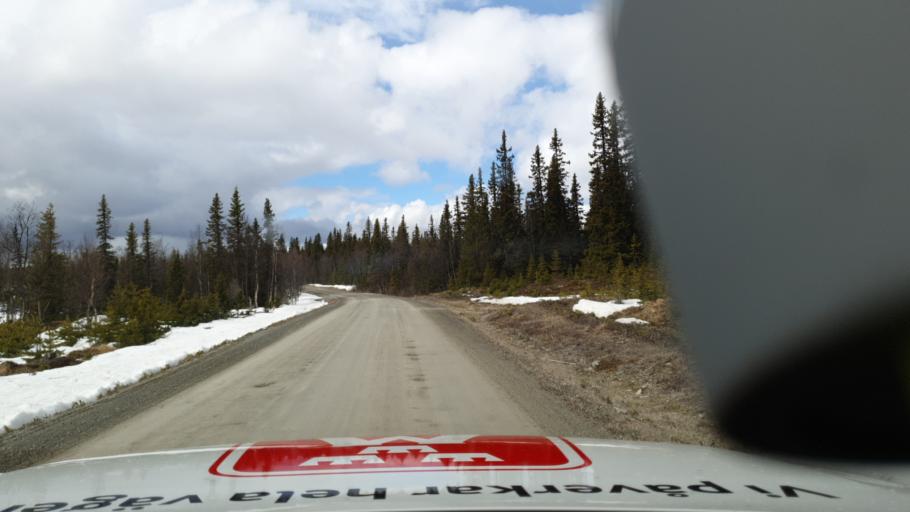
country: SE
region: Jaemtland
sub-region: Bergs Kommun
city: Hoverberg
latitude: 62.8551
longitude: 13.8992
